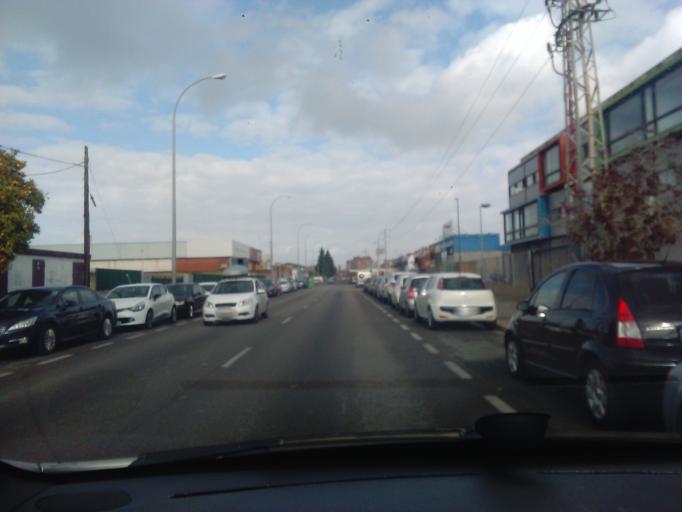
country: ES
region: Andalusia
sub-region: Provincia de Sevilla
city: Sevilla
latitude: 37.3782
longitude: -5.9257
